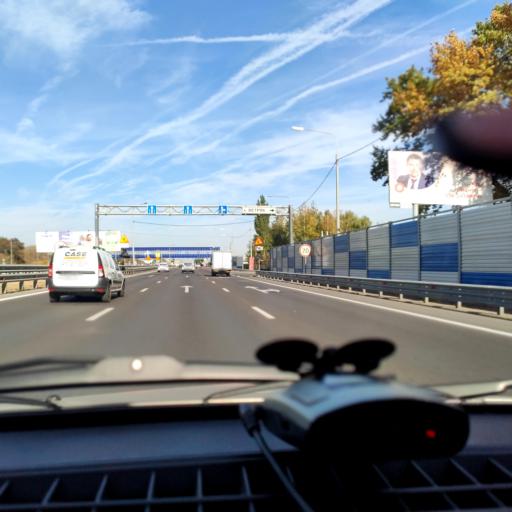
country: RU
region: Voronezj
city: Podgornoye
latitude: 51.7689
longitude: 39.1915
